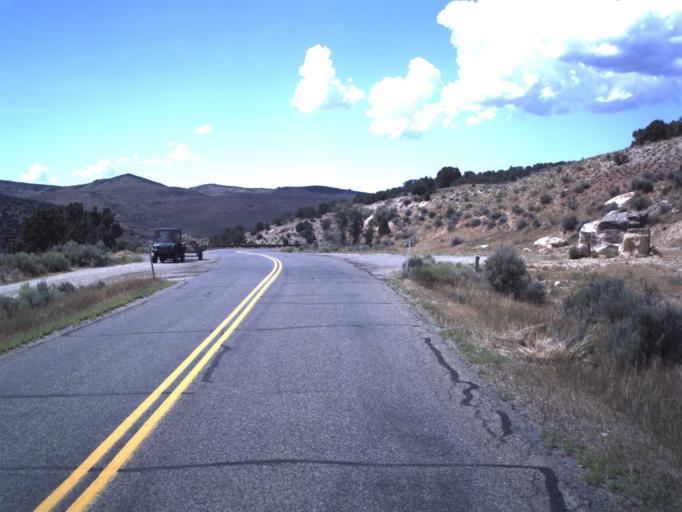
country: US
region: Utah
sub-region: Summit County
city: Oakley
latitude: 40.7633
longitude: -111.3804
